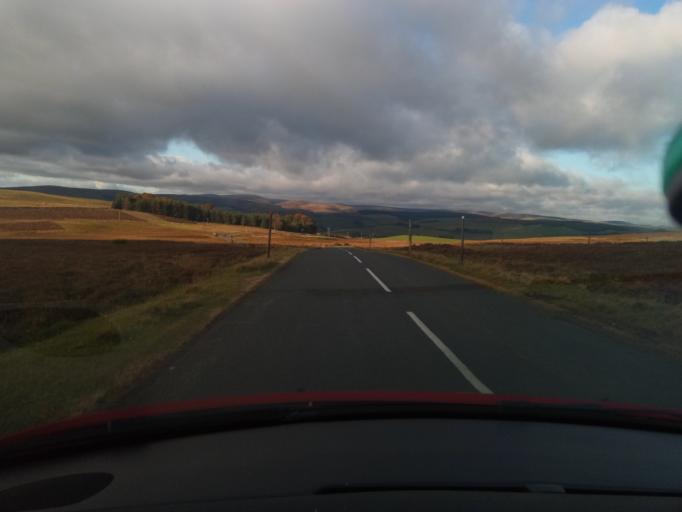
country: GB
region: Scotland
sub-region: The Scottish Borders
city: Lauder
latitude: 55.7014
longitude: -2.8182
